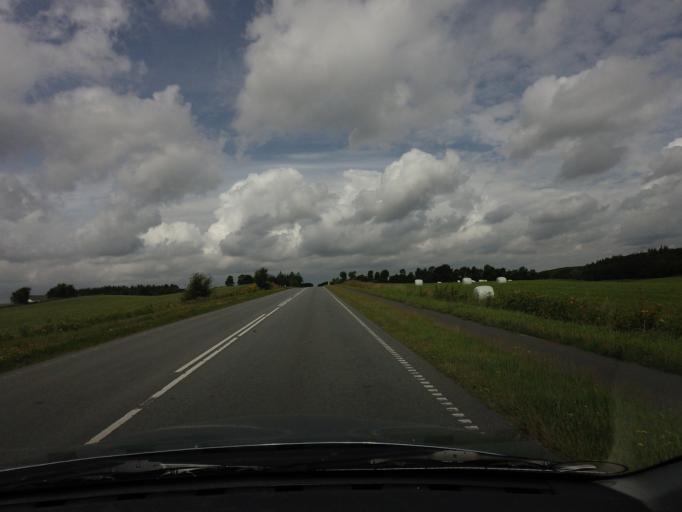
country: DK
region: North Denmark
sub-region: Hjorring Kommune
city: Tars
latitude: 57.3774
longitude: 10.1530
